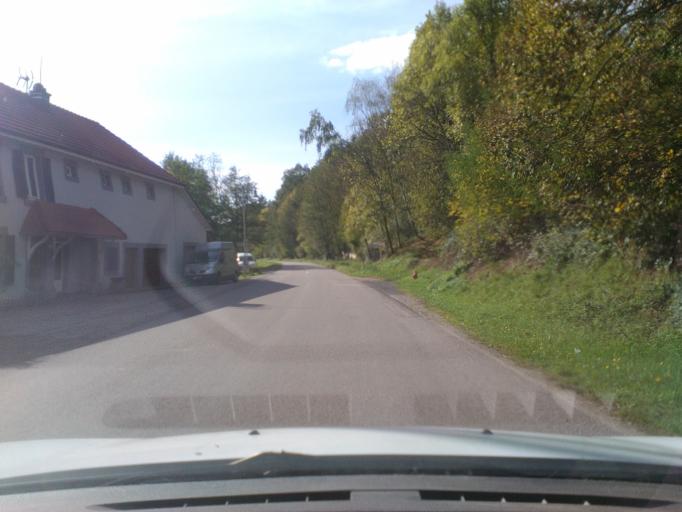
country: FR
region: Lorraine
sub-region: Departement des Vosges
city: Ban-de-Laveline
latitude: 48.2923
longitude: 7.0598
